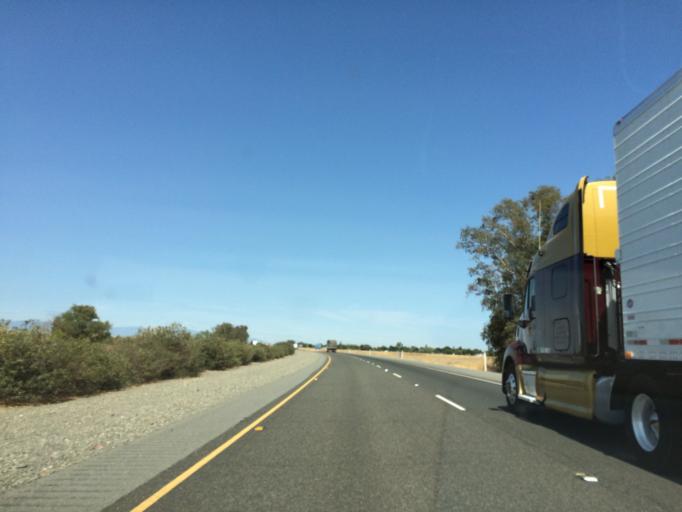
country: US
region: California
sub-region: Glenn County
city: Willows
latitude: 39.5012
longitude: -122.2001
